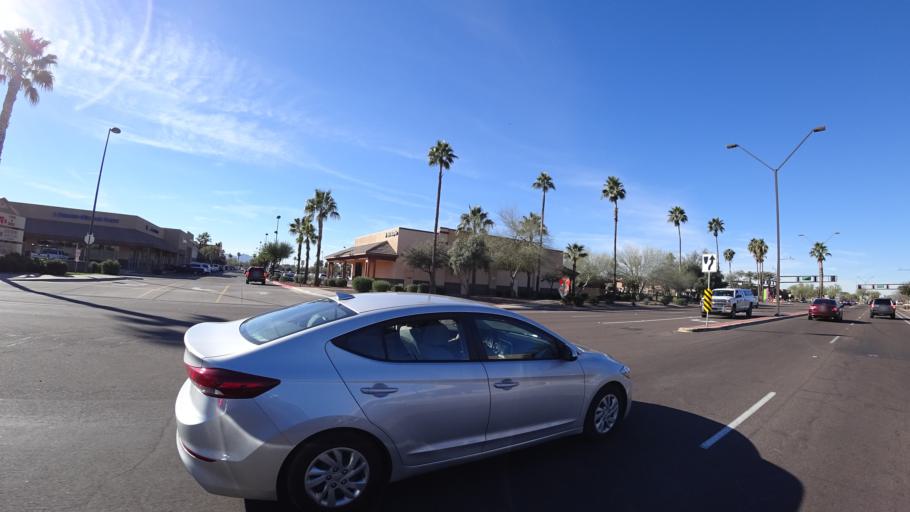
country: US
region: Arizona
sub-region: Maricopa County
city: Avondale
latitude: 33.4643
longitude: -112.3393
